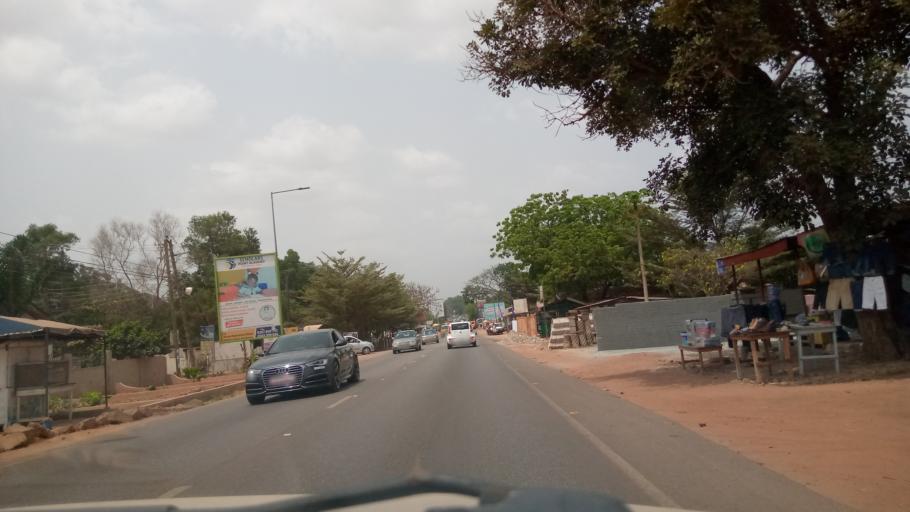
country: GH
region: Greater Accra
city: Dome
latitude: 5.6676
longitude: -0.2118
